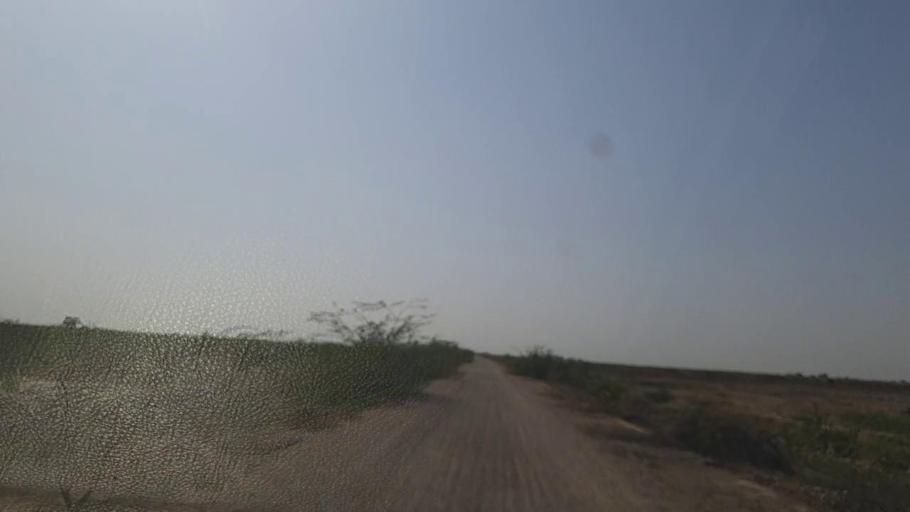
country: PK
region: Sindh
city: Naukot
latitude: 24.5925
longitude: 69.3014
